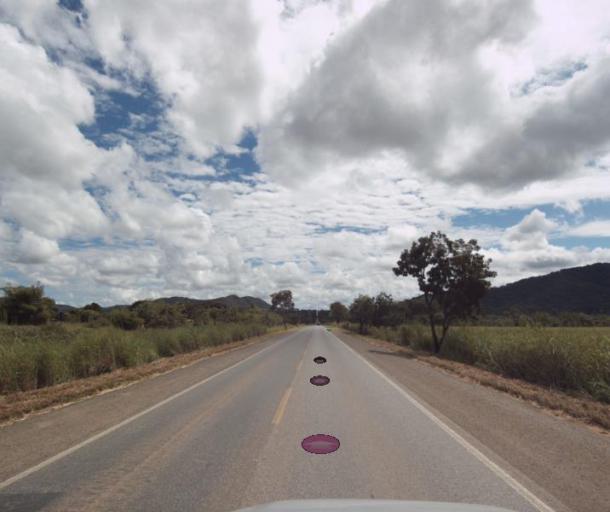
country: BR
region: Goias
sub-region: Uruacu
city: Uruacu
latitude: -14.4266
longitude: -49.1570
